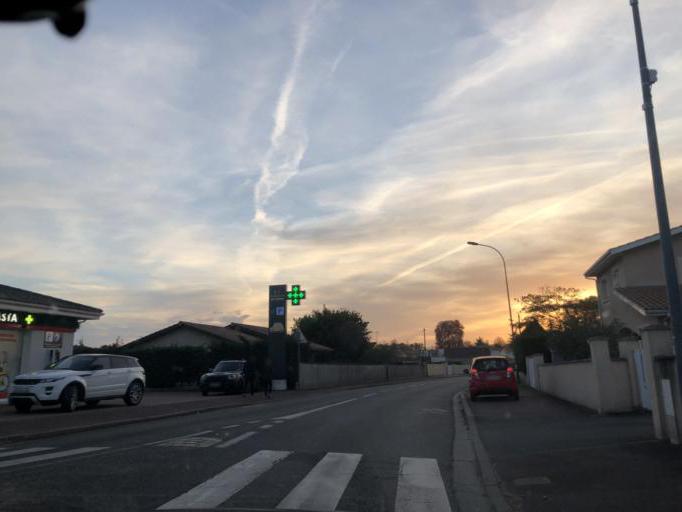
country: FR
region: Aquitaine
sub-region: Departement de la Gironde
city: Le Bouscat
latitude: 44.8837
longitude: -0.5940
